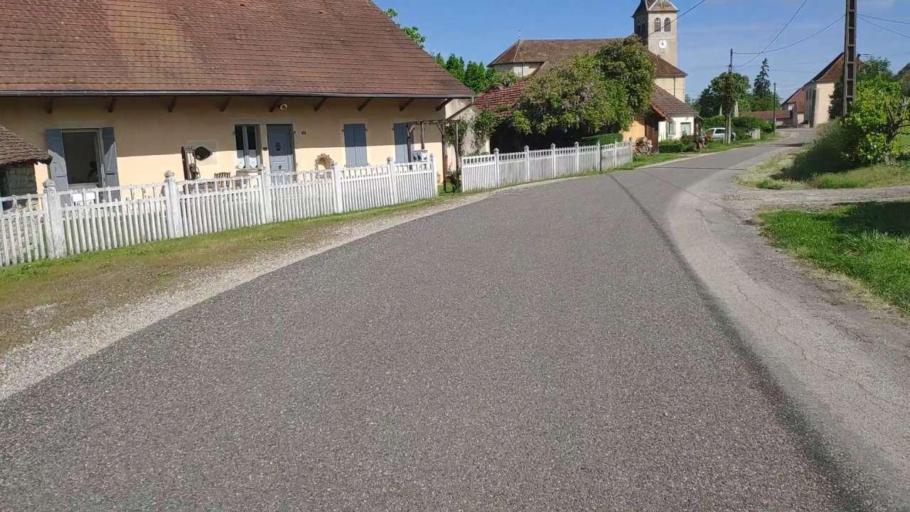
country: FR
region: Franche-Comte
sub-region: Departement du Jura
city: Bletterans
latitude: 46.7106
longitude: 5.4538
